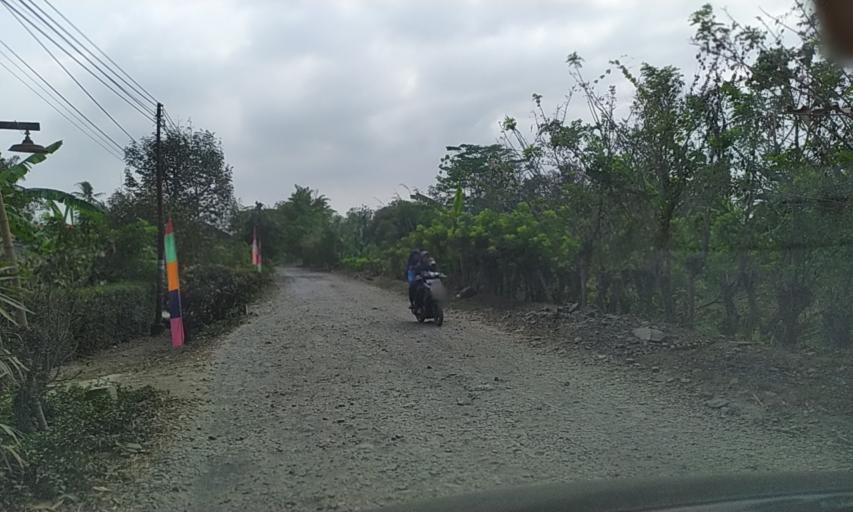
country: ID
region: Central Java
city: Madusari
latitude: -7.6306
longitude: 109.0768
